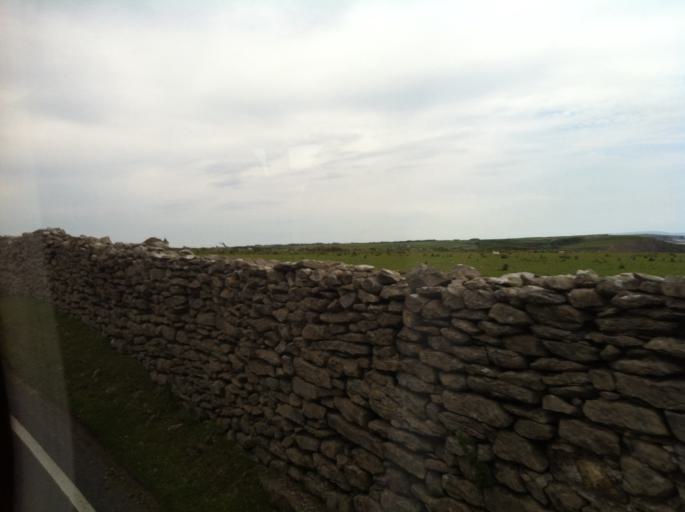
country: GB
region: Wales
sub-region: Bridgend county borough
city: Merthyr Mawr
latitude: 51.4533
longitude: -3.6172
